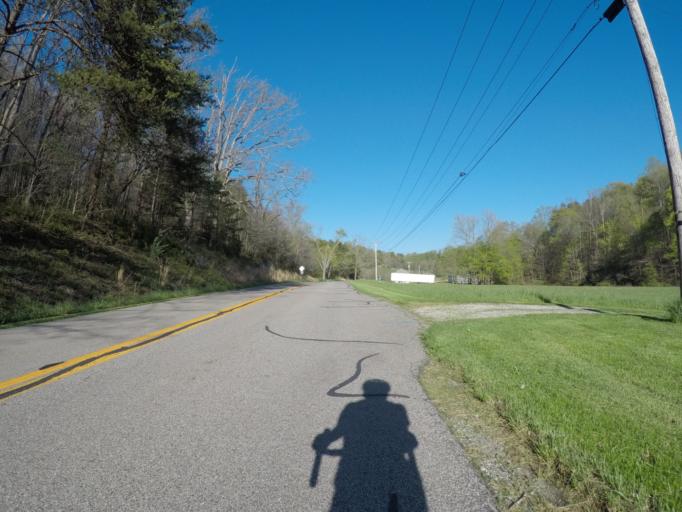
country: US
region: Kentucky
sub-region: Boyd County
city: Meads
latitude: 38.3634
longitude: -82.6757
